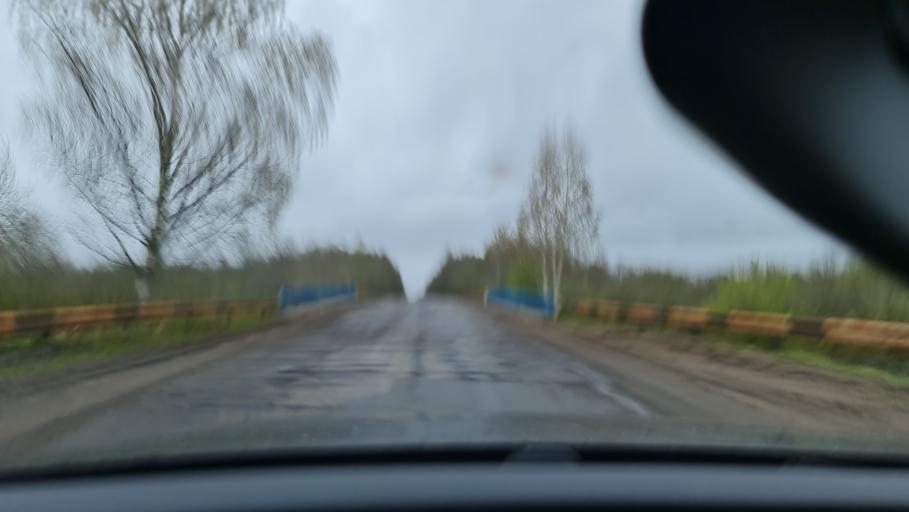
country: RU
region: Novgorod
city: Demyansk
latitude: 57.7421
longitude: 32.5727
